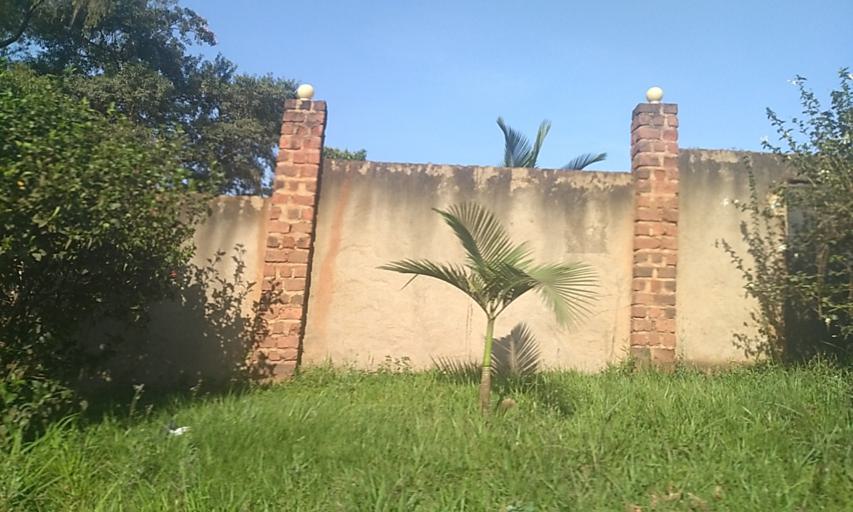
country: UG
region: Central Region
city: Kampala Central Division
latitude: 0.3157
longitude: 32.5534
